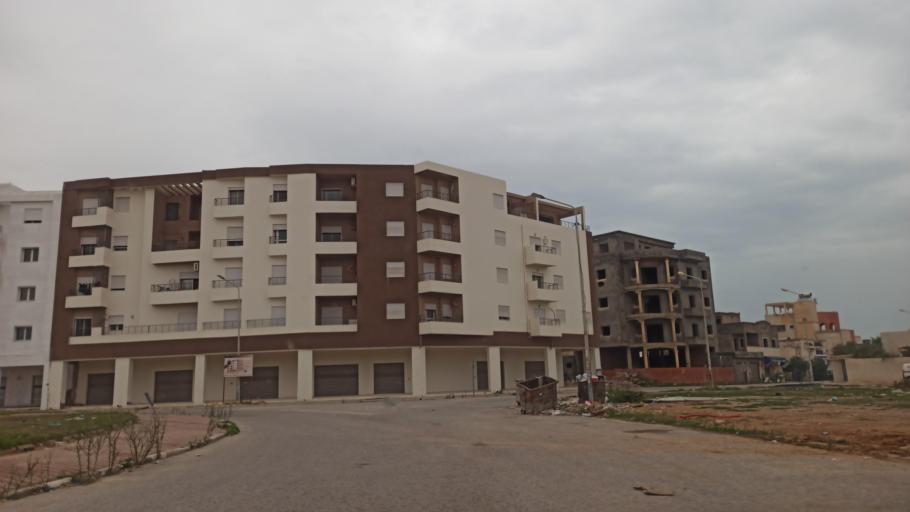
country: TN
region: Tunis
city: Hammam-Lif
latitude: 36.7053
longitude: 10.4141
